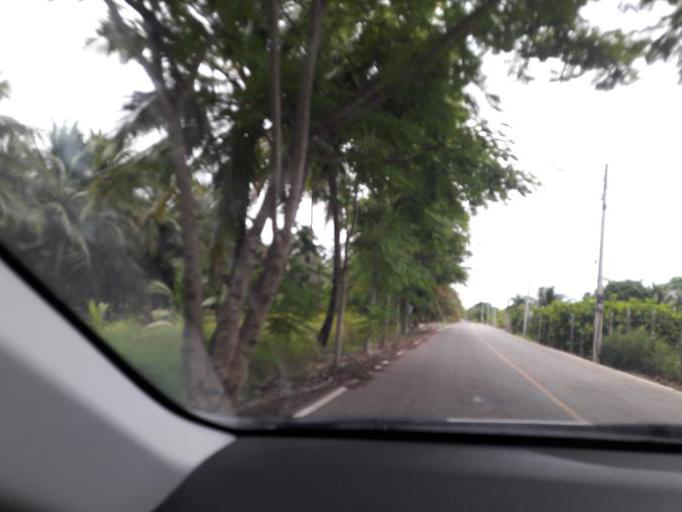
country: TH
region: Ratchaburi
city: Damnoen Saduak
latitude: 13.5482
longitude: 99.9796
